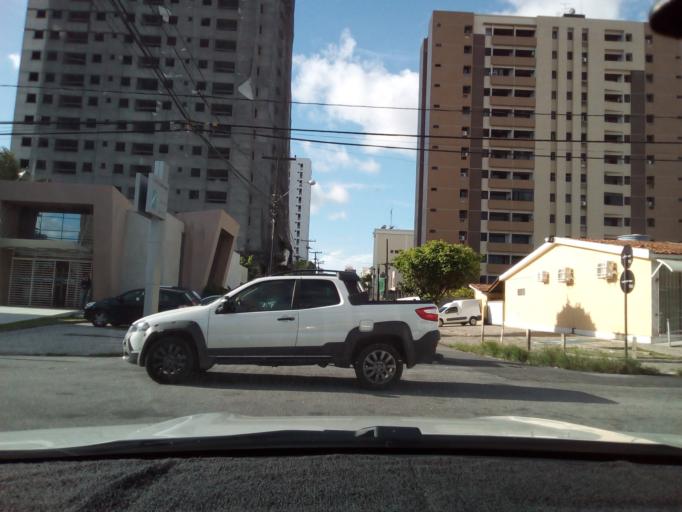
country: BR
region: Paraiba
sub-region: Joao Pessoa
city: Joao Pessoa
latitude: -7.1226
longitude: -34.8533
